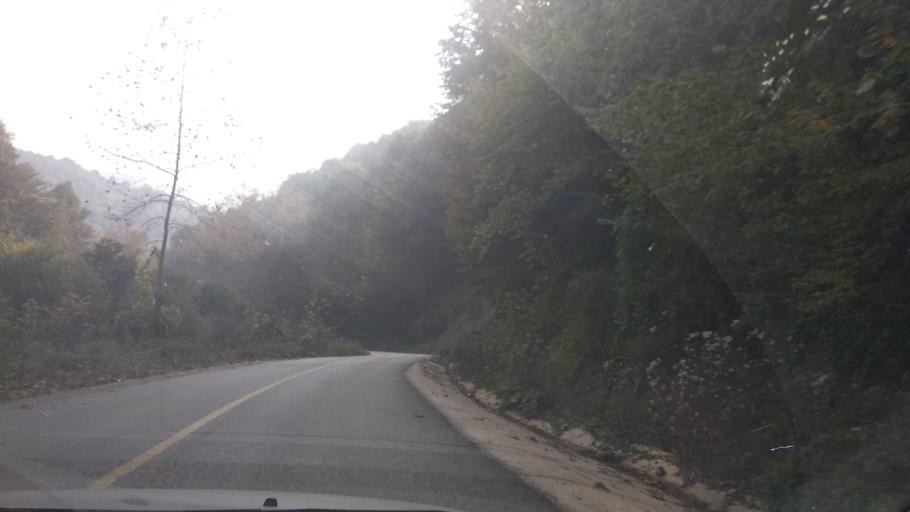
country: TR
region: Duzce
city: Kaynasli
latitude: 40.7144
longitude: 31.2648
